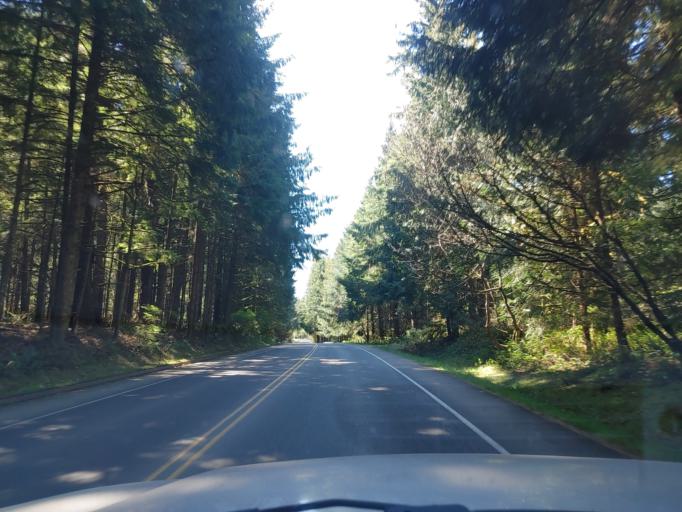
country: US
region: Oregon
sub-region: Clatsop County
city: Warrenton
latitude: 46.1369
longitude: -123.8802
